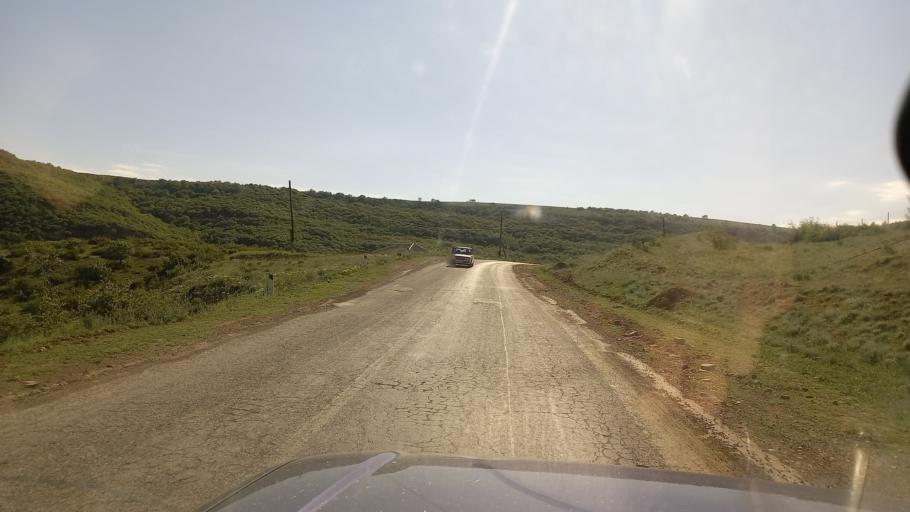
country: RU
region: Dagestan
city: Chinar
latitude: 41.9553
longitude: 48.1350
